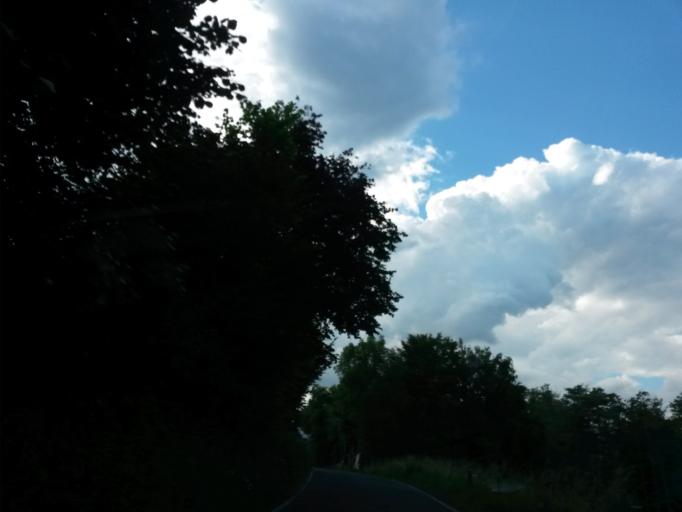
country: DE
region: North Rhine-Westphalia
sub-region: Regierungsbezirk Koln
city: Overath
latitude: 50.8905
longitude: 7.2953
